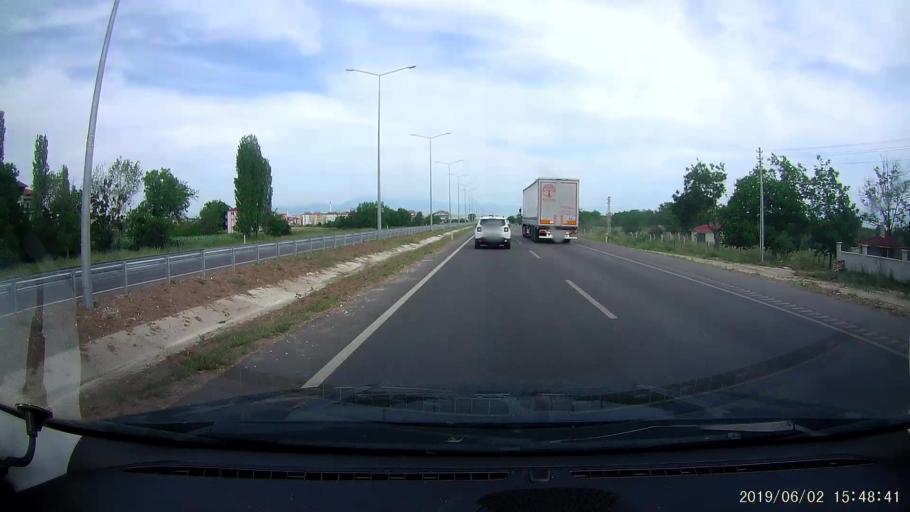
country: TR
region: Amasya
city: Merzifon
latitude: 40.8612
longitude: 35.4463
